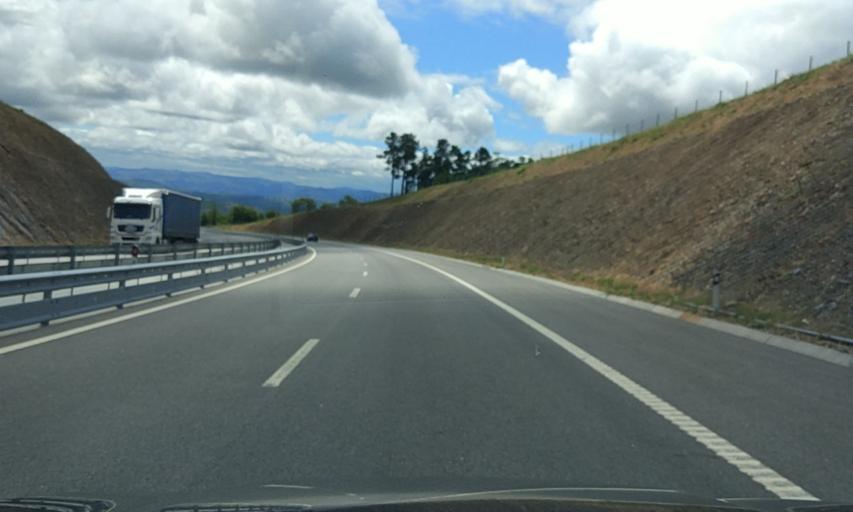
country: PT
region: Vila Real
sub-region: Santa Marta de Penaguiao
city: Santa Marta de Penaguiao
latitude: 41.2712
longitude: -7.8131
